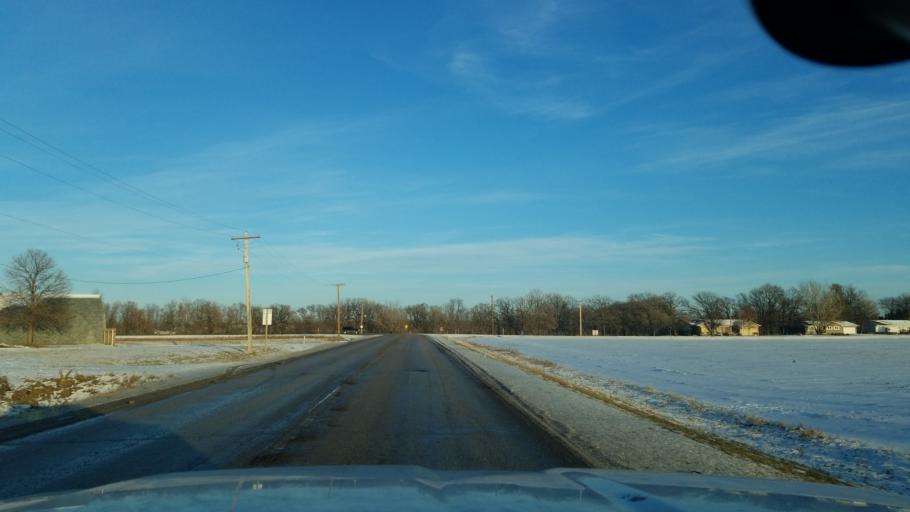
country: CA
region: Manitoba
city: Portage la Prairie
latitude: 49.9570
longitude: -98.3226
